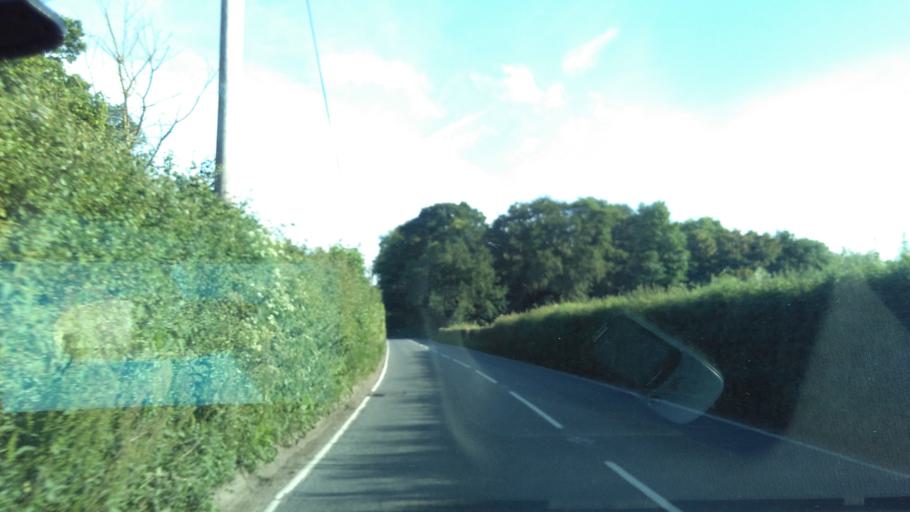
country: GB
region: England
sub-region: Kent
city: Faversham
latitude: 51.2670
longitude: 0.8810
